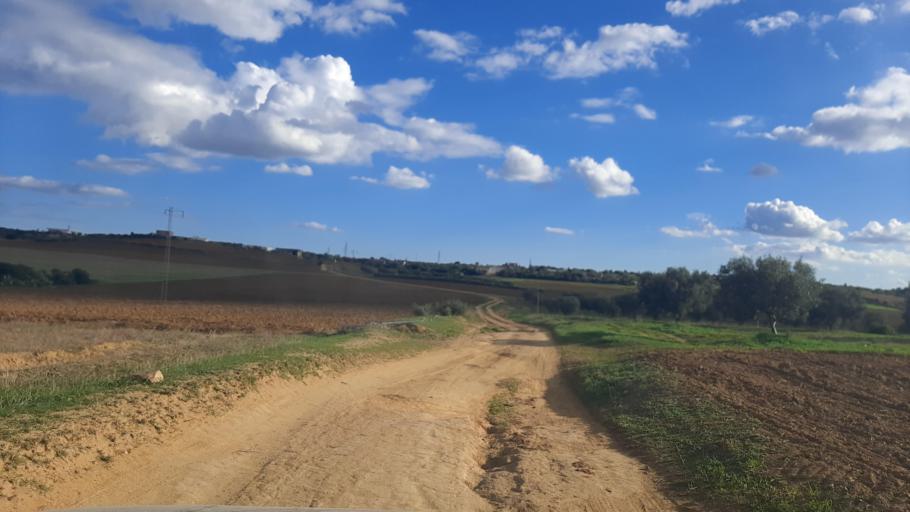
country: TN
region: Nabul
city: Bu `Urqub
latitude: 36.4467
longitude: 10.5020
